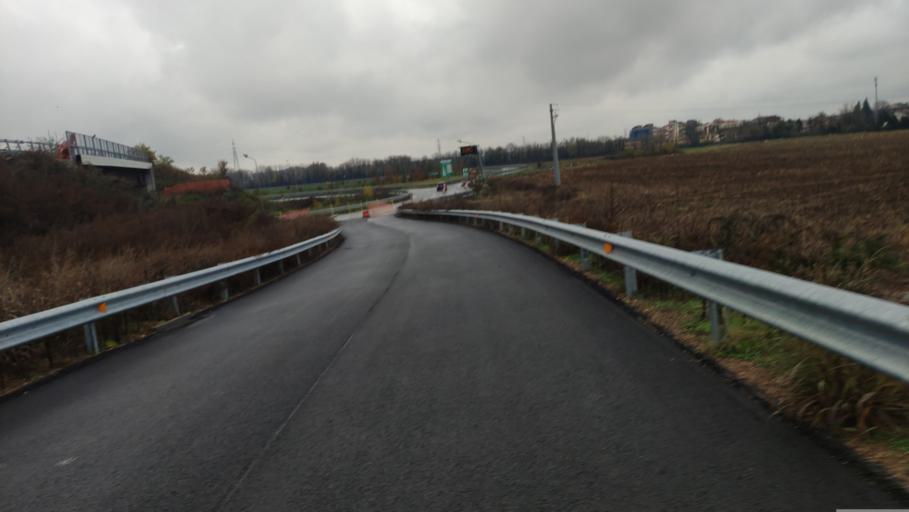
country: IT
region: Lombardy
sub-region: Citta metropolitana di Milano
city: Passirana
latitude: 45.5544
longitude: 9.0383
